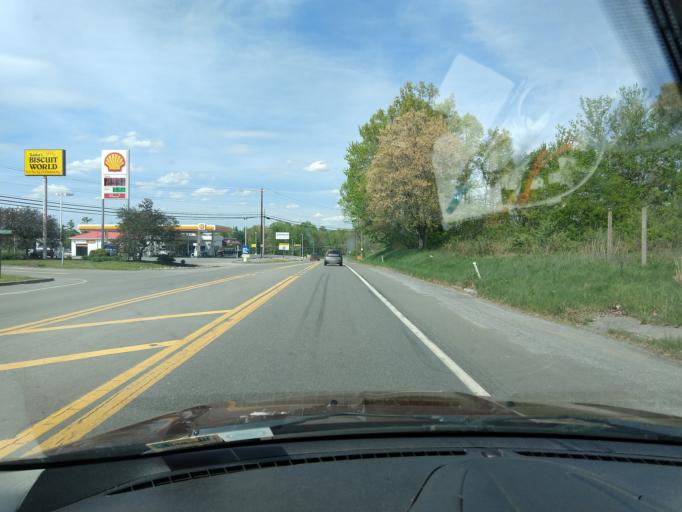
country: US
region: West Virginia
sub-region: Raleigh County
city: Daniels
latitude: 37.7708
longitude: -81.1216
